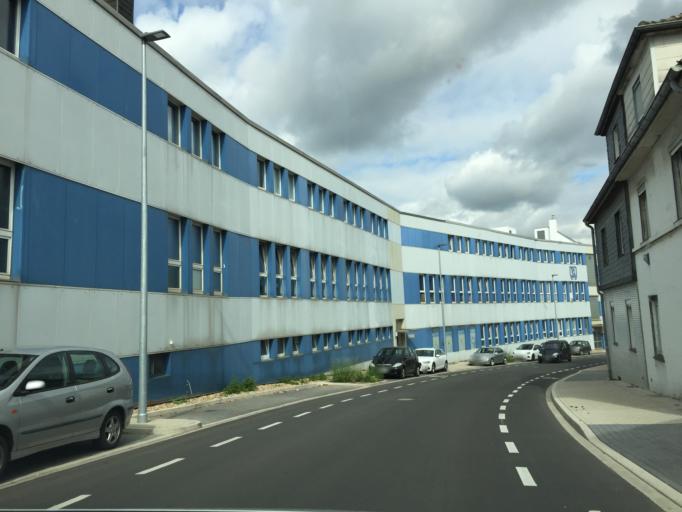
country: DE
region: North Rhine-Westphalia
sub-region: Regierungsbezirk Dusseldorf
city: Heiligenhaus
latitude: 51.3264
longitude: 6.9545
